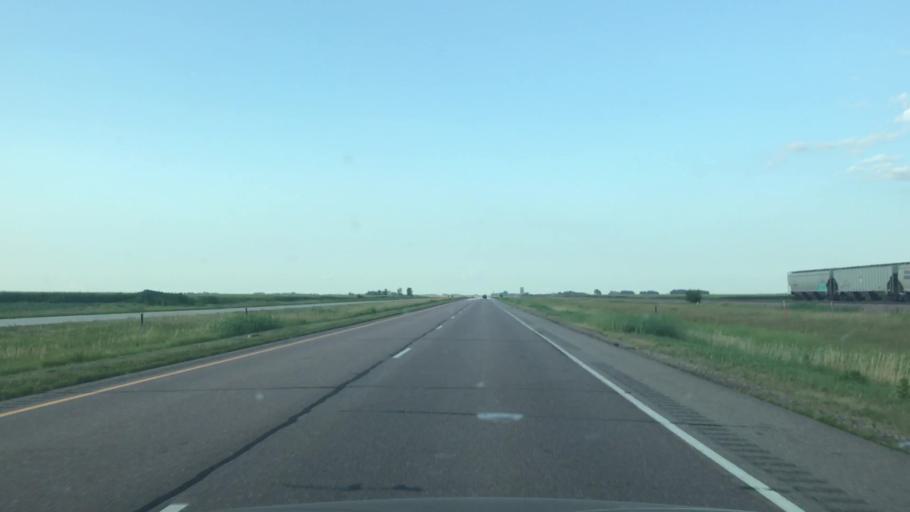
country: US
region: Minnesota
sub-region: Nobles County
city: Worthington
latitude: 43.7265
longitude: -95.4286
